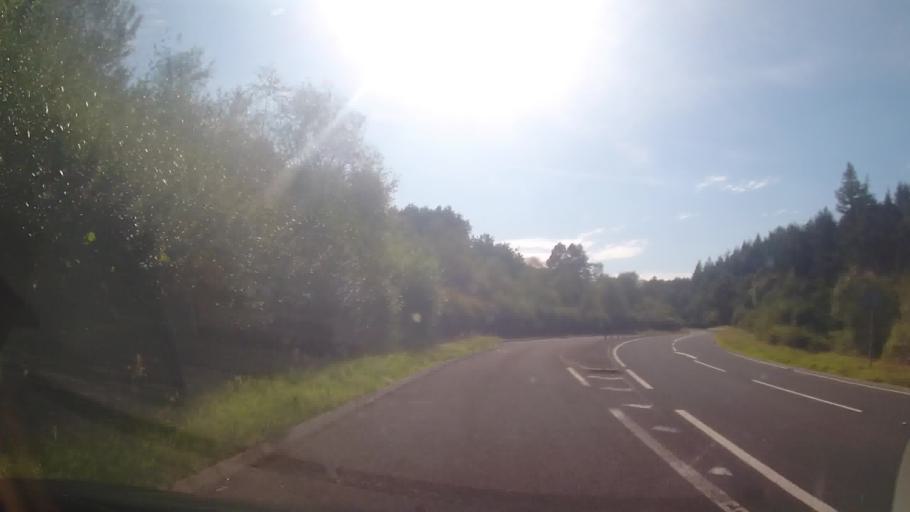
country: GB
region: Wales
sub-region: Sir Powys
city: Mochdre
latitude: 52.4334
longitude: -3.3433
